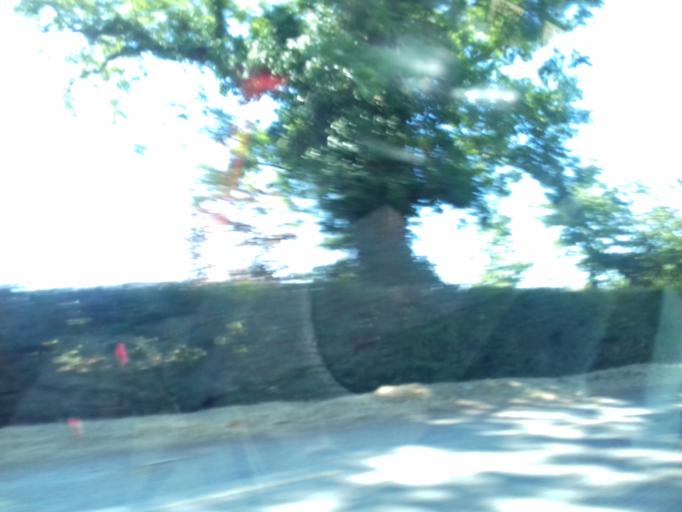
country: IE
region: Leinster
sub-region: An Mhi
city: Stamullin
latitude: 53.5437
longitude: -6.2724
